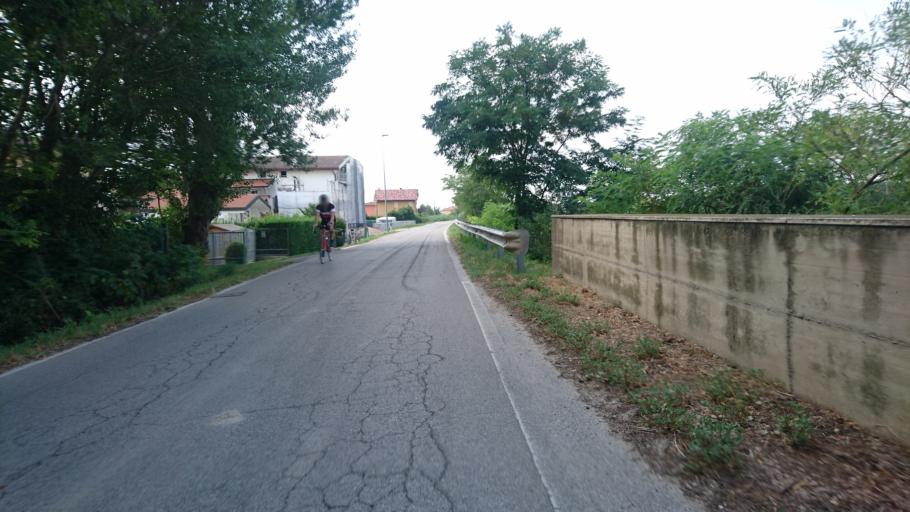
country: IT
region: Veneto
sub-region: Provincia di Venezia
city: Sant'Anna
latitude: 45.1620
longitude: 12.2697
